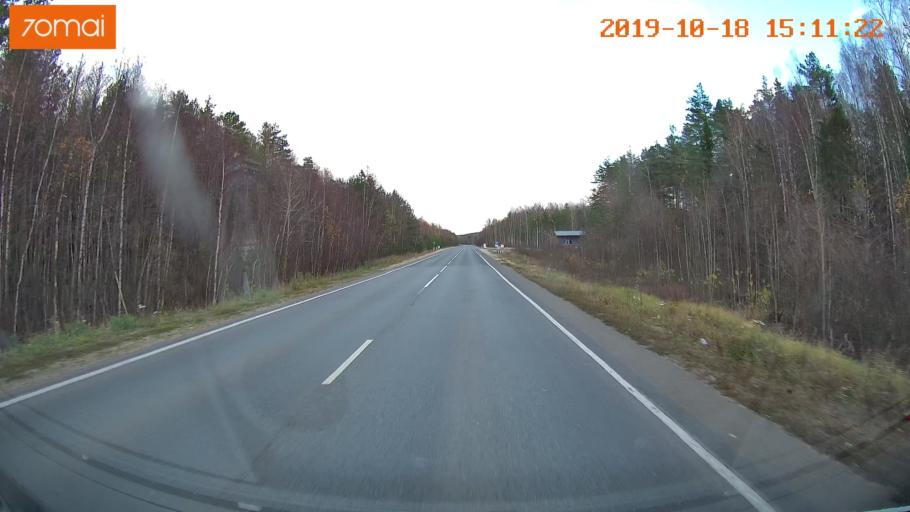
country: RU
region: Vladimir
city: Gus'-Khrustal'nyy
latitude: 55.5713
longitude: 40.6693
